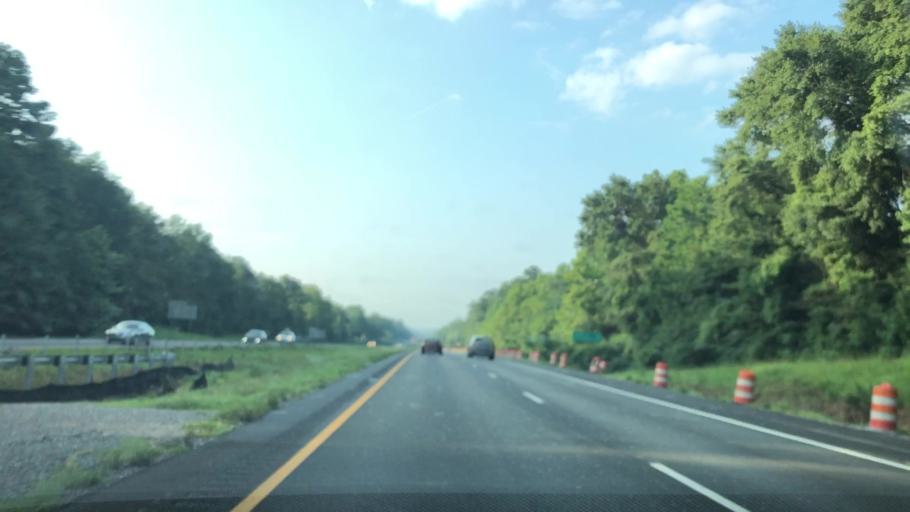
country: US
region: Alabama
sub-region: Chilton County
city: Clanton
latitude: 32.8327
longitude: -86.5916
